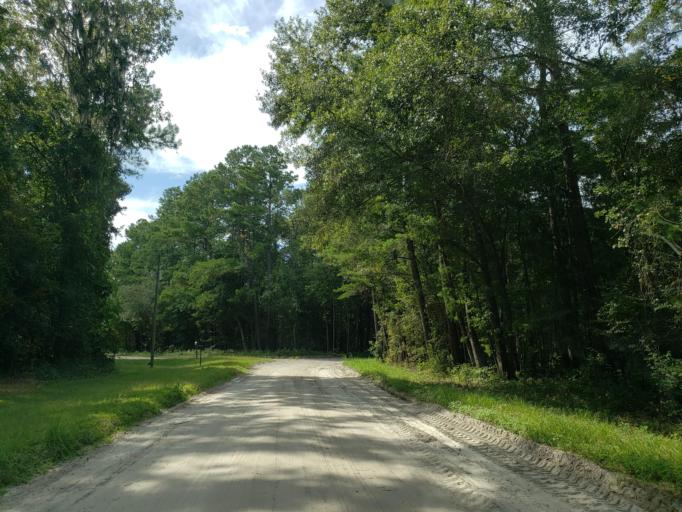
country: US
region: Florida
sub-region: Hamilton County
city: Jasper
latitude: 30.5509
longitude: -83.0866
